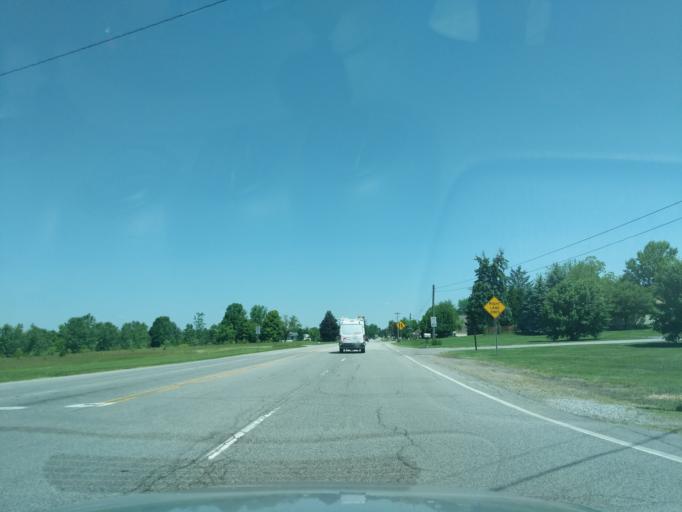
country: US
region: Indiana
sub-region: Whitley County
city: Columbia City
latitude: 41.1702
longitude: -85.4915
